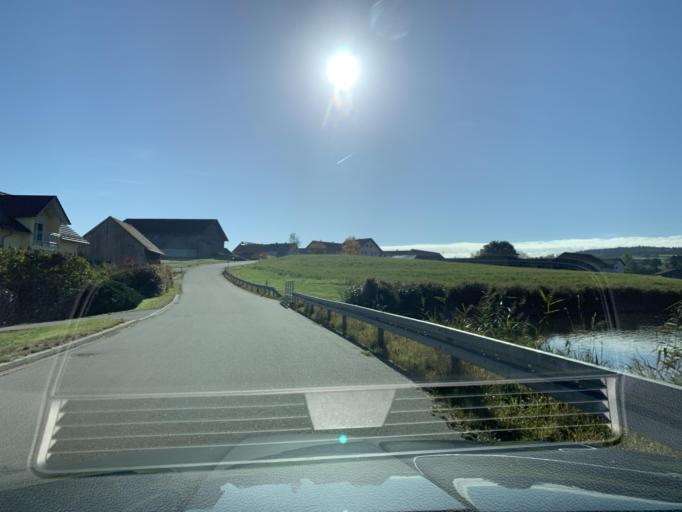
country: DE
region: Bavaria
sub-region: Upper Palatinate
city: Thanstein
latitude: 49.3866
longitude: 12.4790
